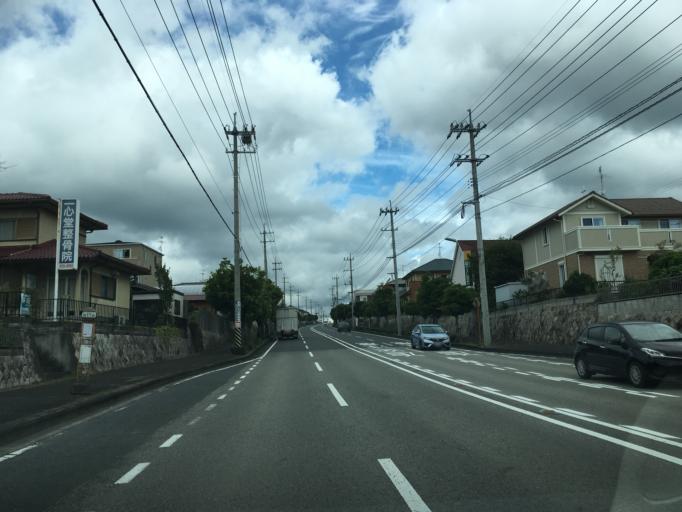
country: JP
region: Okayama
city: Okayama-shi
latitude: 34.7765
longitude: 134.0383
